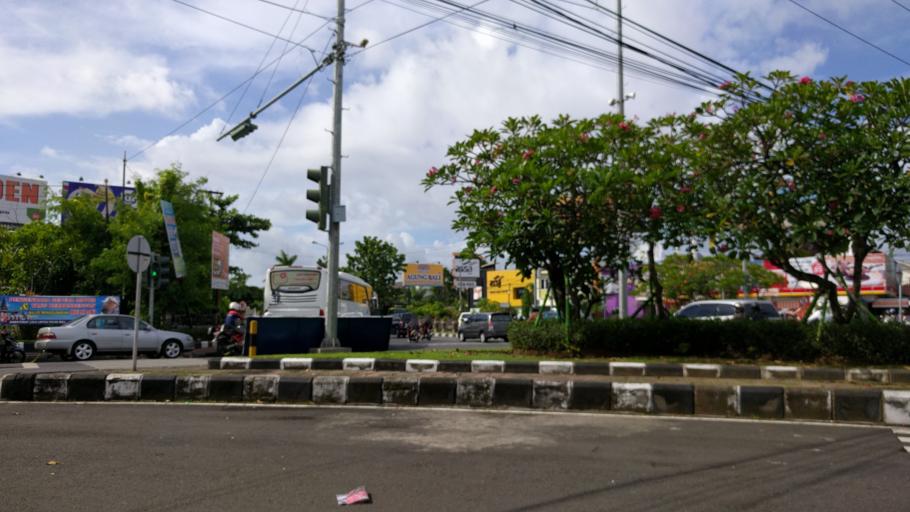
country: ID
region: Bali
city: Kuta
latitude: -8.7057
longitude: 115.1827
